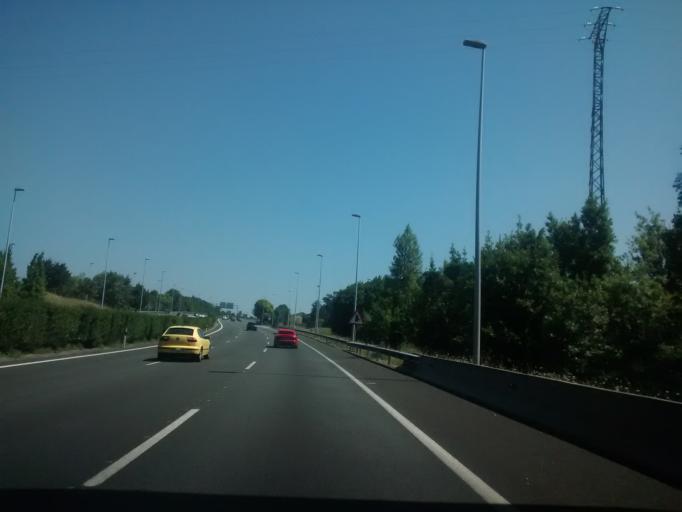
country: ES
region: Cantabria
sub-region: Provincia de Cantabria
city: Entrambasaguas
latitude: 43.3888
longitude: -3.6649
